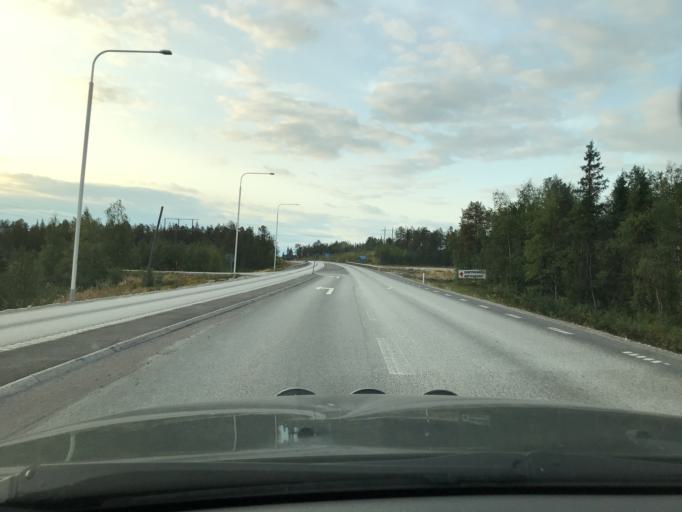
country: SE
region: Norrbotten
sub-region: Gallivare Kommun
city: Malmberget
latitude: 67.6513
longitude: 21.0181
